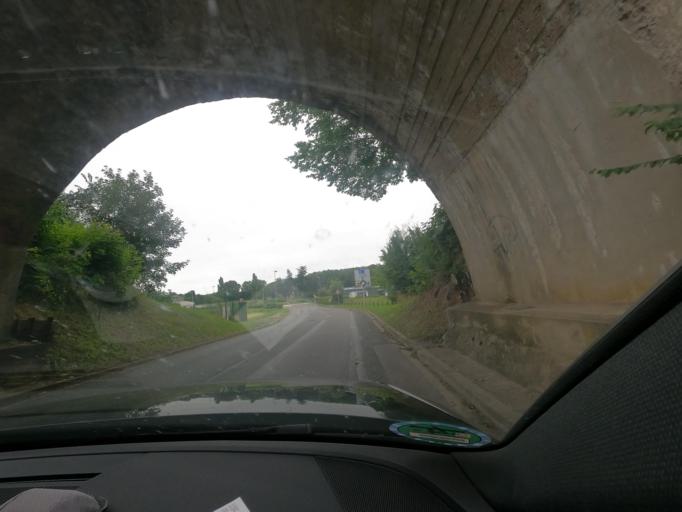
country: FR
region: Picardie
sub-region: Departement de l'Oise
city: Ressons-sur-Matz
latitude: 49.5352
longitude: 2.7408
